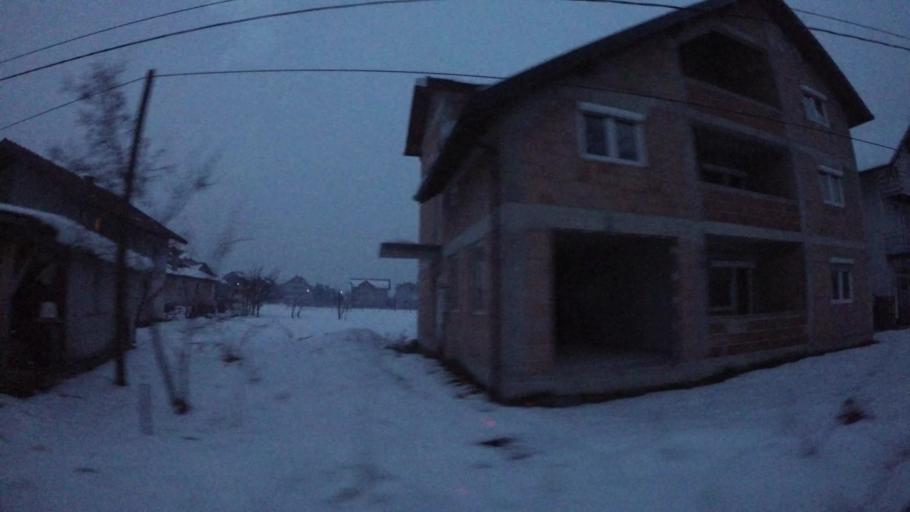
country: BA
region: Federation of Bosnia and Herzegovina
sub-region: Kanton Sarajevo
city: Sarajevo
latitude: 43.8542
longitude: 18.2936
